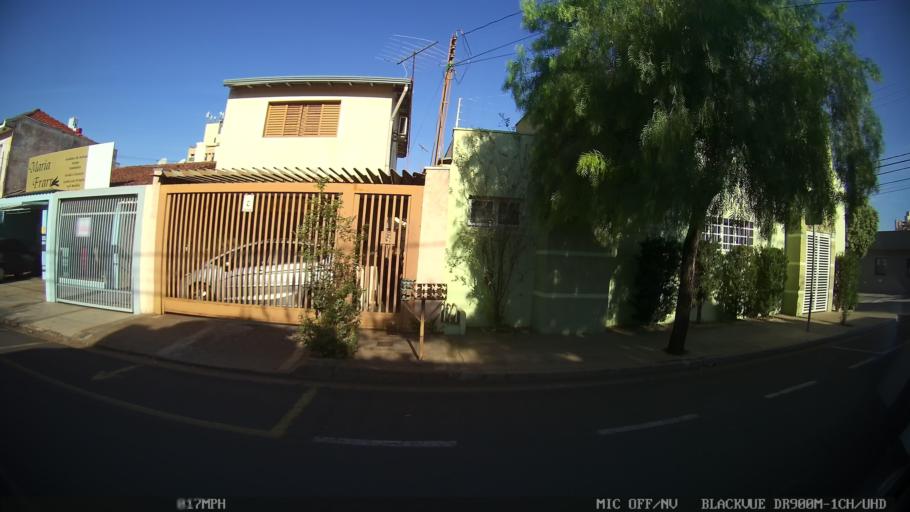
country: BR
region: Sao Paulo
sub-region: Sao Jose Do Rio Preto
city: Sao Jose do Rio Preto
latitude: -20.8083
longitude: -49.3868
